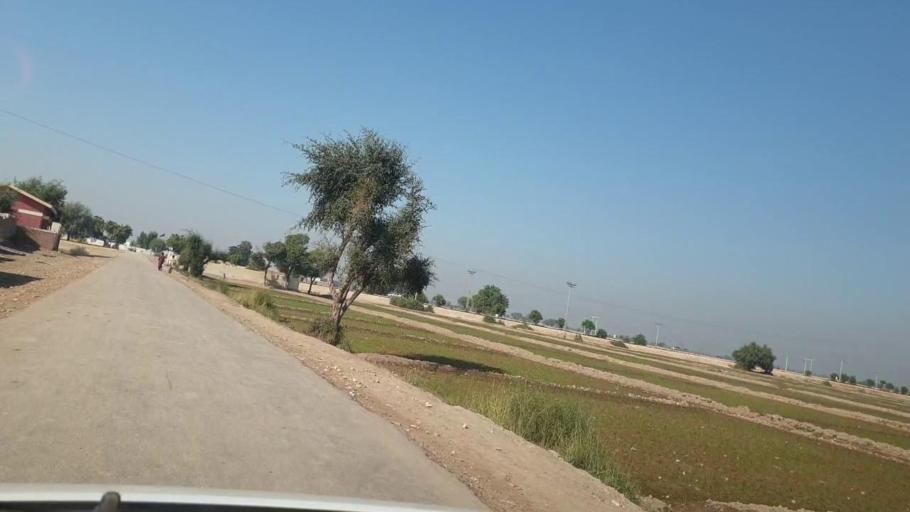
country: PK
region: Sindh
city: Bhan
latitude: 26.6104
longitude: 67.7343
